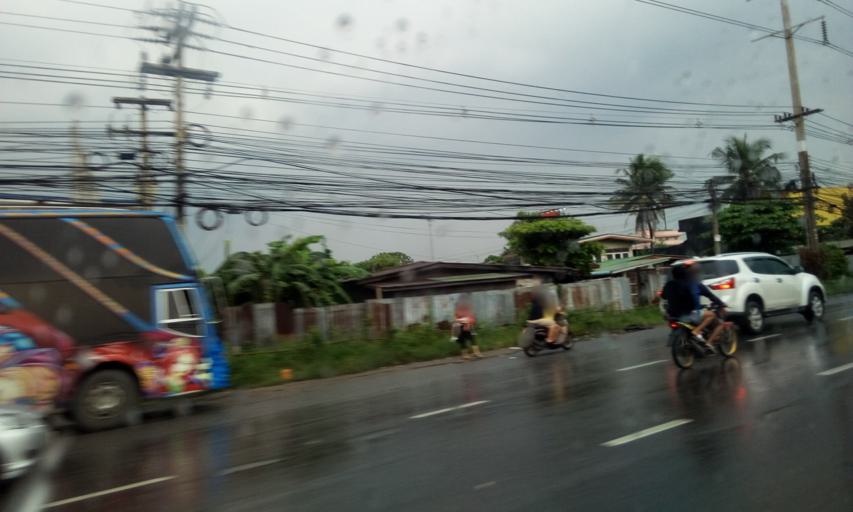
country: TH
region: Bangkok
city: Sai Mai
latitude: 13.9884
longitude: 100.6312
